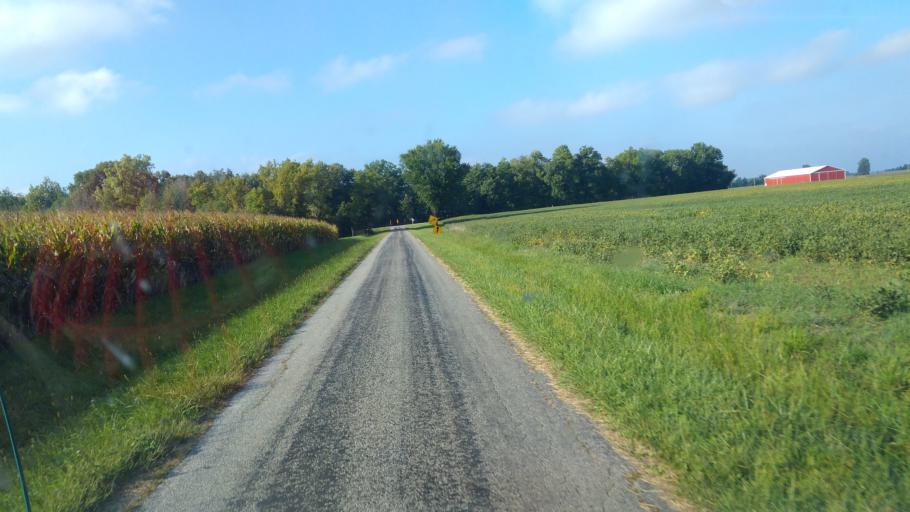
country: US
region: Ohio
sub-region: Wyandot County
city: Upper Sandusky
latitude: 40.7697
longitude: -83.3620
